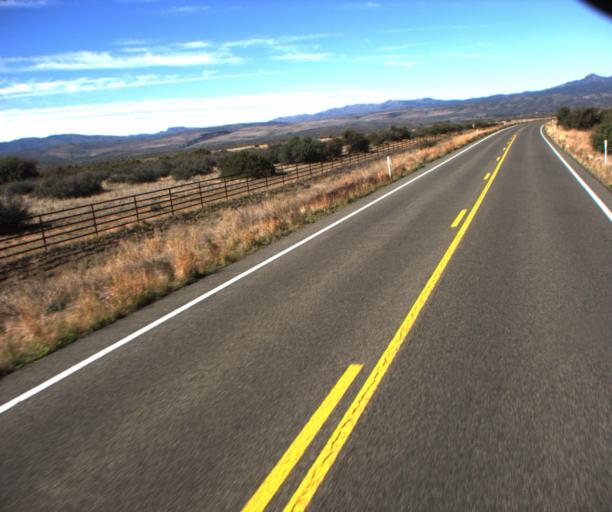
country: US
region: Arizona
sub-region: Yavapai County
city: Prescott
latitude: 34.3916
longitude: -112.6381
